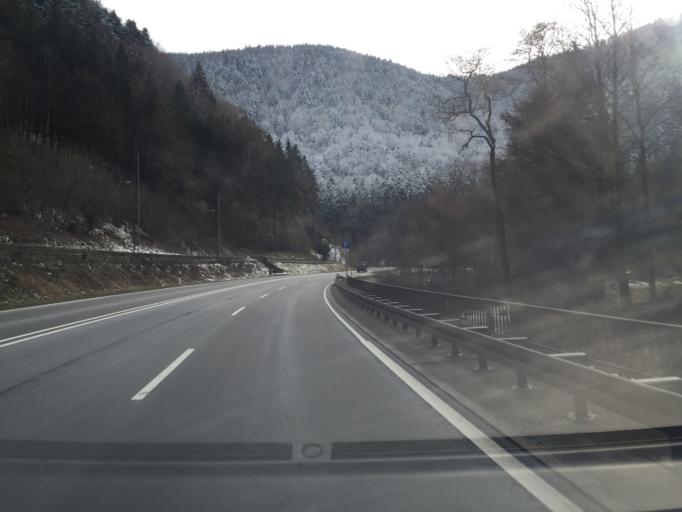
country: DE
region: Baden-Wuerttemberg
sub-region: Freiburg Region
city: Buchenbach
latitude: 47.9294
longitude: 8.0320
